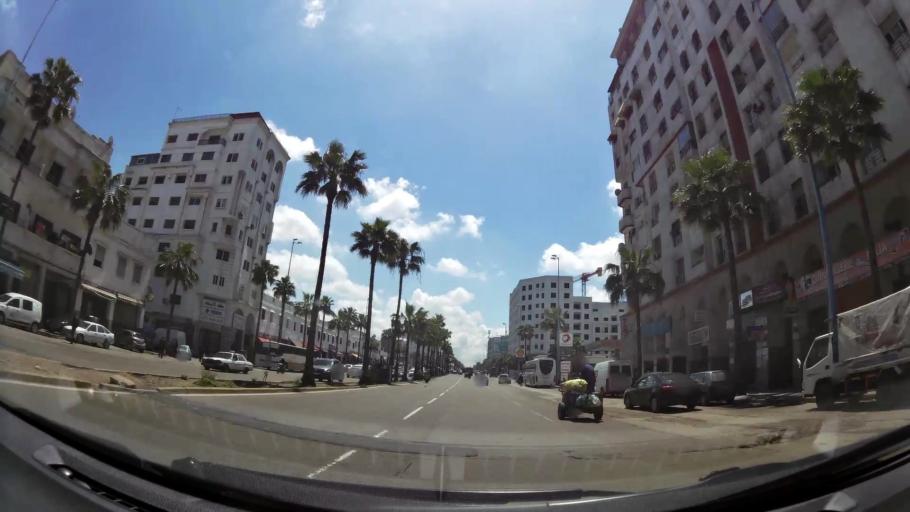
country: MA
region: Grand Casablanca
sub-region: Casablanca
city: Casablanca
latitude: 33.5690
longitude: -7.5961
